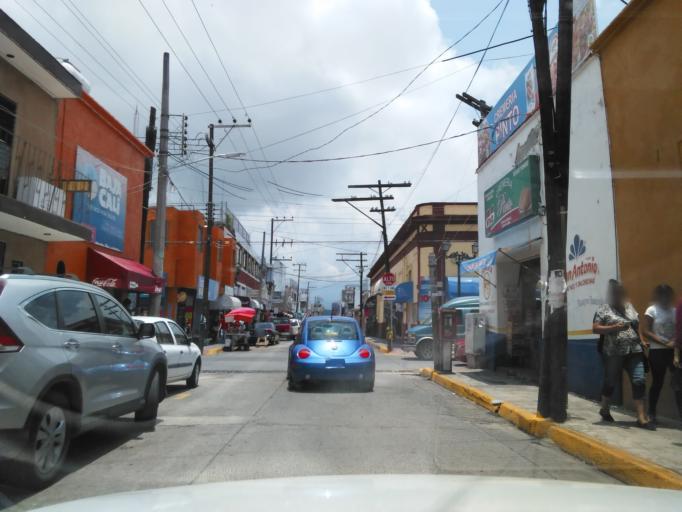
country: MX
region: Nayarit
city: Tepic
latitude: 21.5114
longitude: -104.8959
